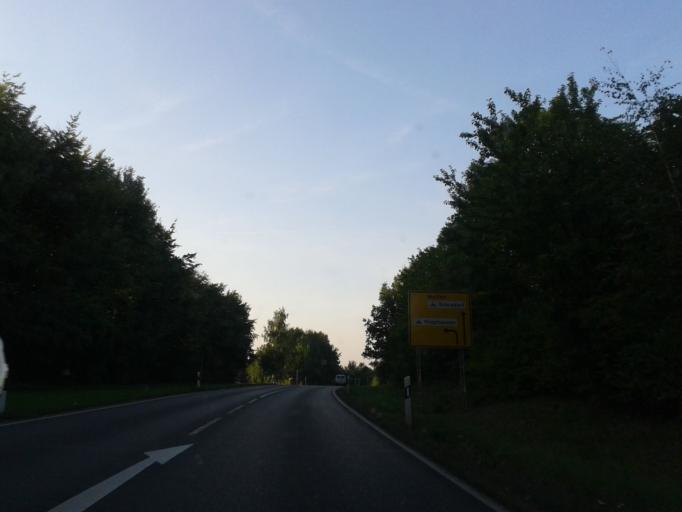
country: DE
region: Saxony
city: Wilsdruff
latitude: 51.0654
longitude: 13.5194
